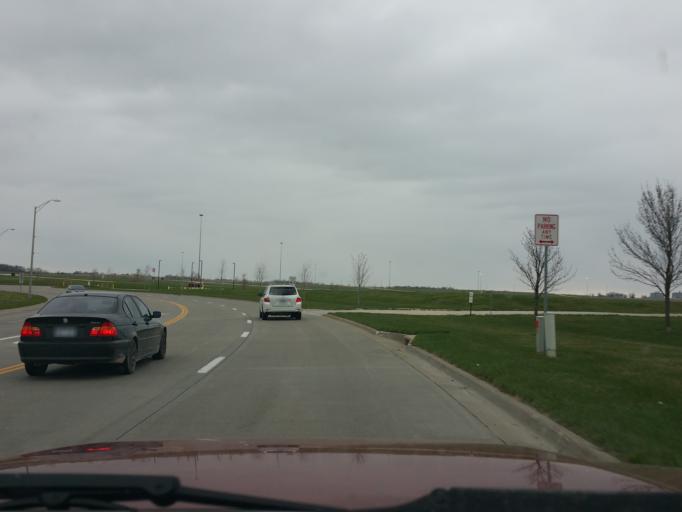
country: US
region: Kansas
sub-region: Wyandotte County
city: Edwardsville
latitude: 39.1087
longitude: -94.8354
